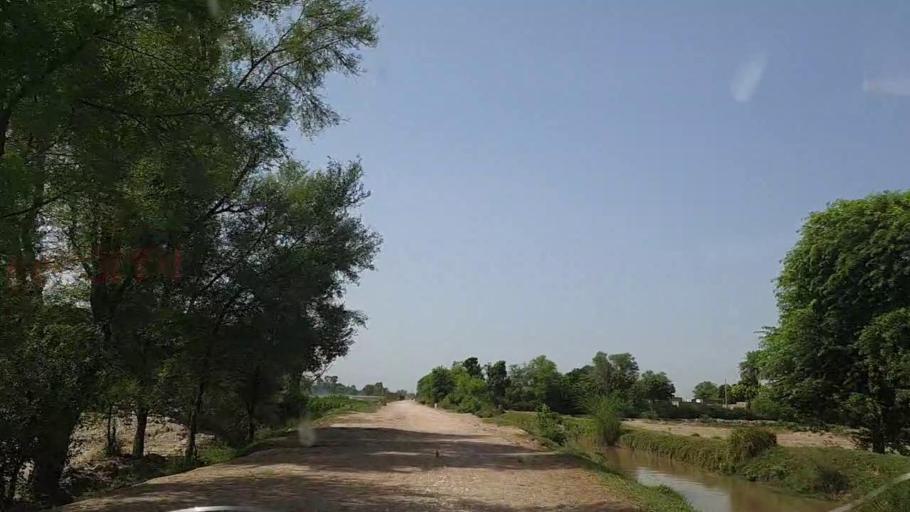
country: PK
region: Sindh
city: Naushahro Firoz
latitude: 26.8586
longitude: 68.0295
